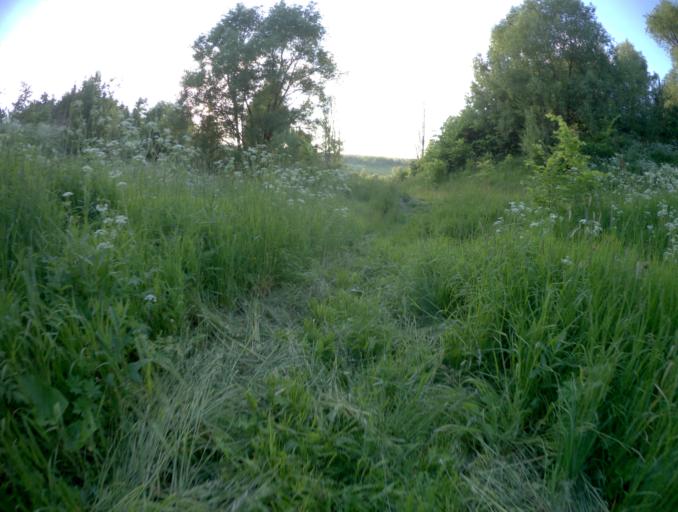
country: RU
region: Vladimir
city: Stavrovo
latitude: 56.2926
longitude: 39.9477
